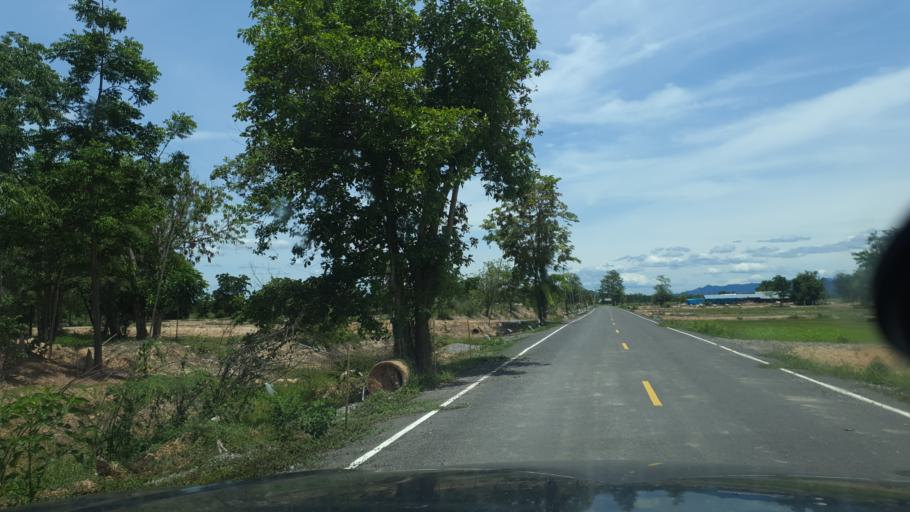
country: TH
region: Sukhothai
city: Ban Dan Lan Hoi
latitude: 17.1507
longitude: 99.6429
